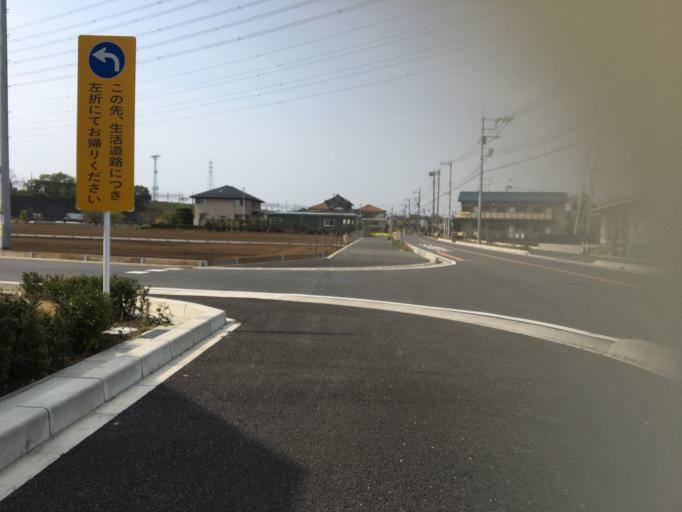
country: JP
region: Saitama
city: Shiki
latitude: 35.8053
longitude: 139.5462
